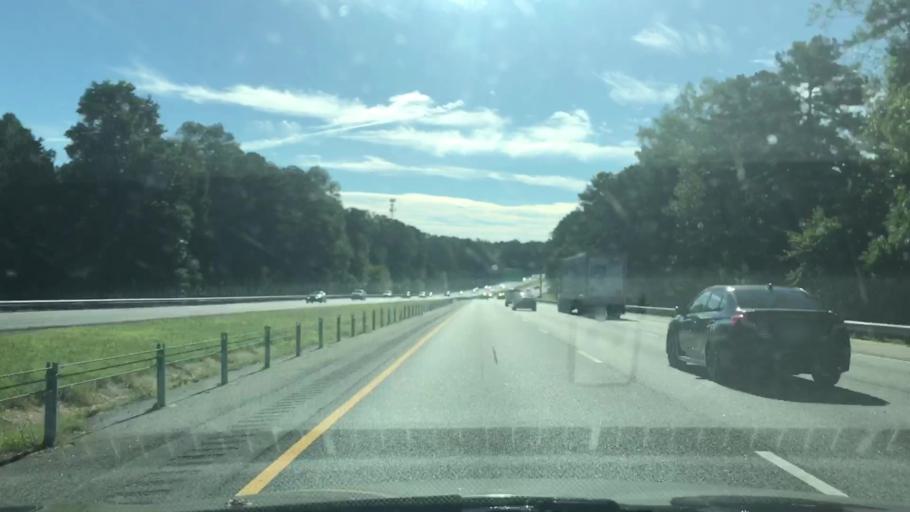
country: US
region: Georgia
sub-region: DeKalb County
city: Stone Mountain
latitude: 33.8325
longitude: -84.1873
